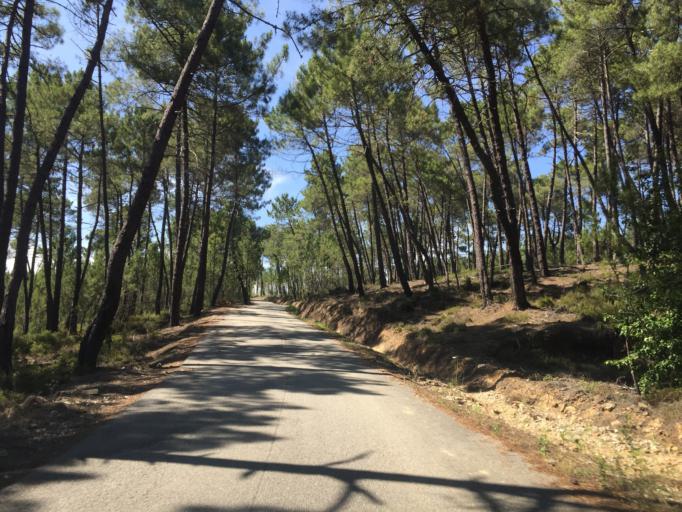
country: PT
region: Castelo Branco
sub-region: Oleiros
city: Oleiros
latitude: 39.9761
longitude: -7.8422
